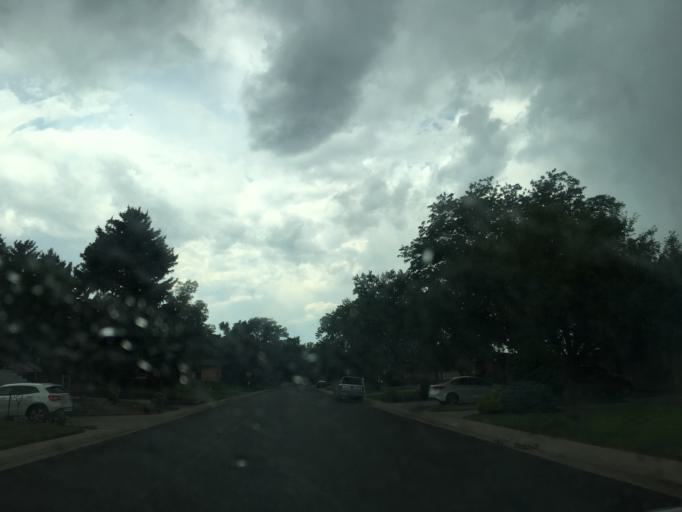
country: US
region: Colorado
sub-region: Arapahoe County
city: Sheridan
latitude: 39.6765
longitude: -105.0446
